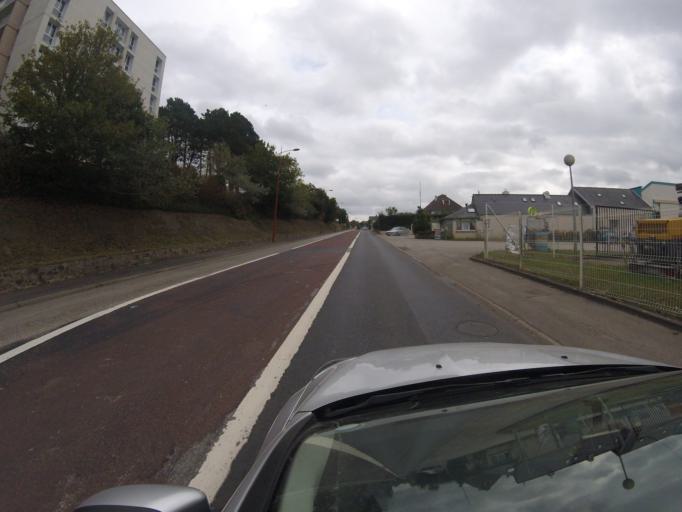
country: FR
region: Lower Normandy
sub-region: Departement de la Manche
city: Cherbourg-Octeville
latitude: 49.6170
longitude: -1.6081
